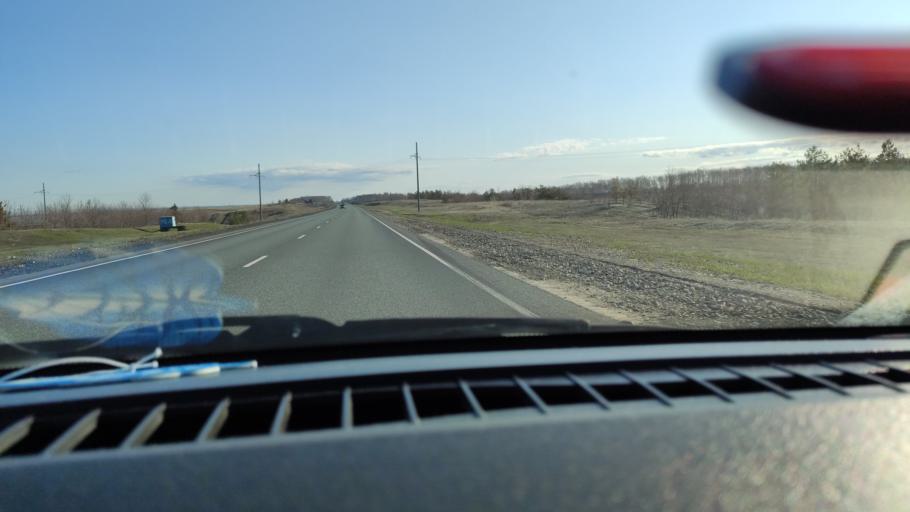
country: RU
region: Saratov
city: Khvalynsk
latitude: 52.5473
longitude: 48.0699
